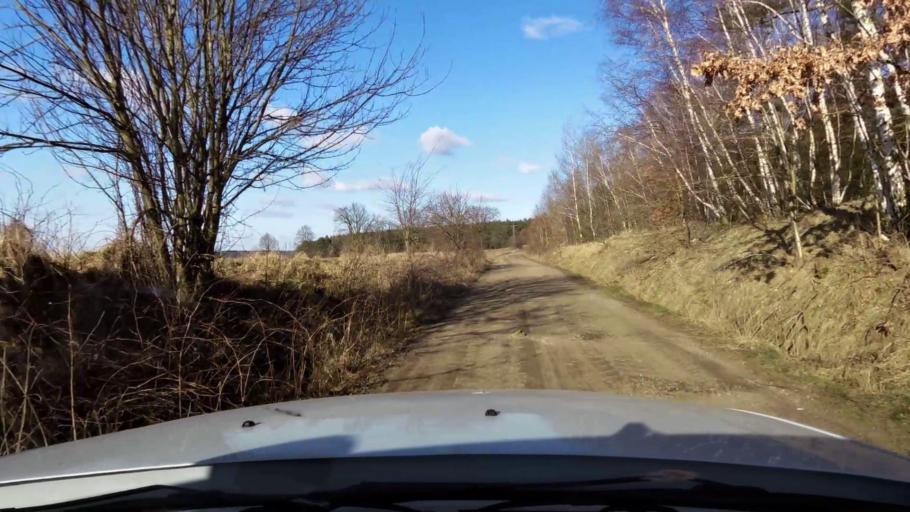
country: PL
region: West Pomeranian Voivodeship
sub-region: Powiat choszczenski
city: Choszczno
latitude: 53.1603
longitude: 15.3776
